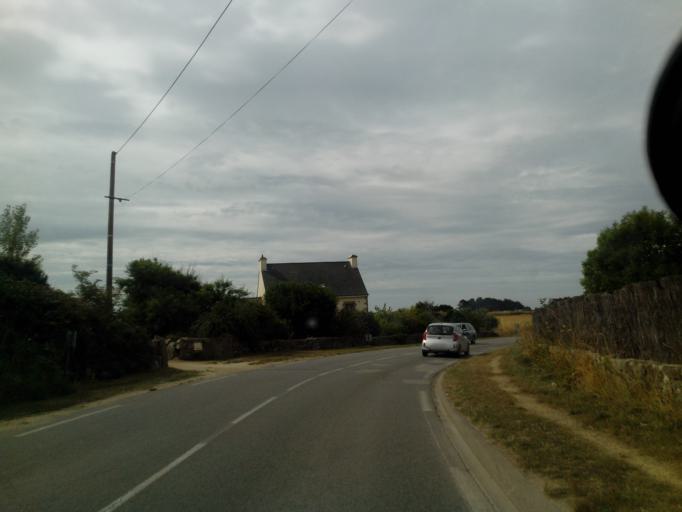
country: FR
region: Brittany
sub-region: Departement du Morbihan
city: Erdeven
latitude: 47.6221
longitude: -3.1617
